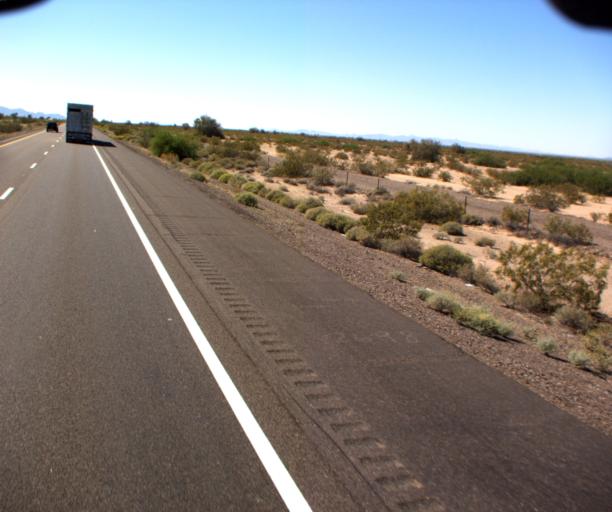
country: US
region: Arizona
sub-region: Yuma County
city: Wellton
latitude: 32.8204
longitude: -113.4760
